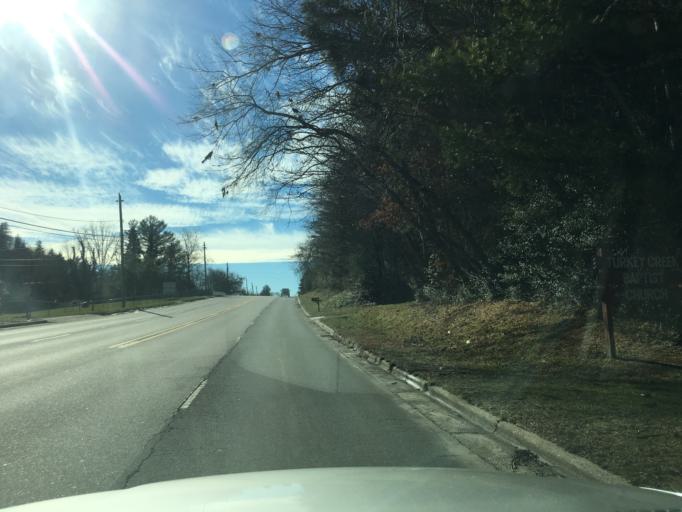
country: US
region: North Carolina
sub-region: Transylvania County
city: Brevard
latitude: 35.2810
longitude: -82.6948
